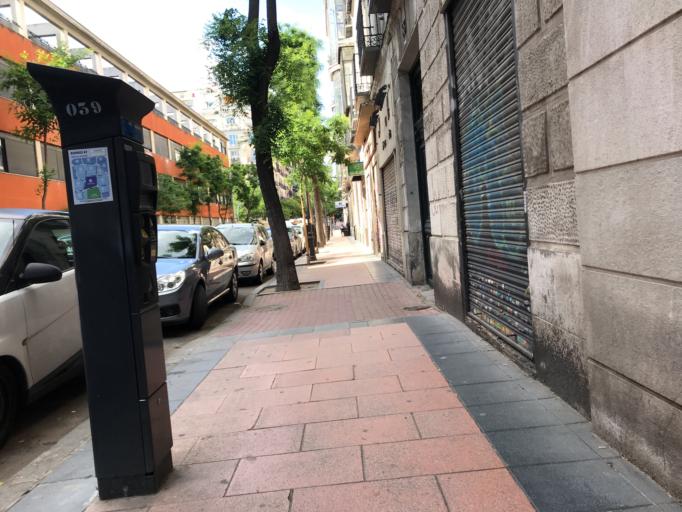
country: ES
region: Madrid
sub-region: Provincia de Madrid
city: Salamanca
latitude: 40.4244
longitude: -3.6855
